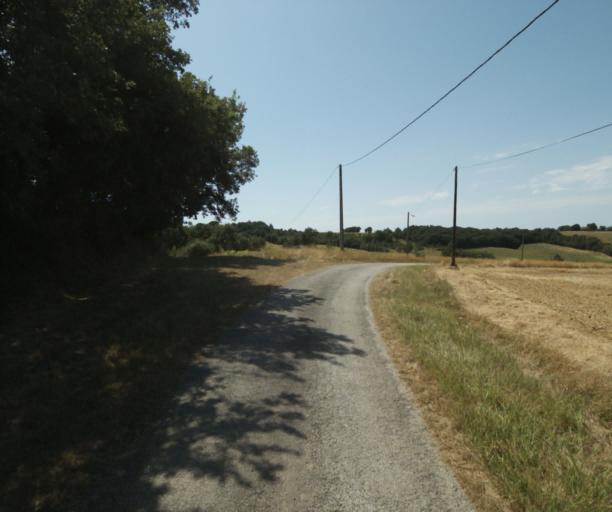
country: FR
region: Midi-Pyrenees
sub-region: Departement de la Haute-Garonne
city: Saint-Felix-Lauragais
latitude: 43.4508
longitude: 1.8659
